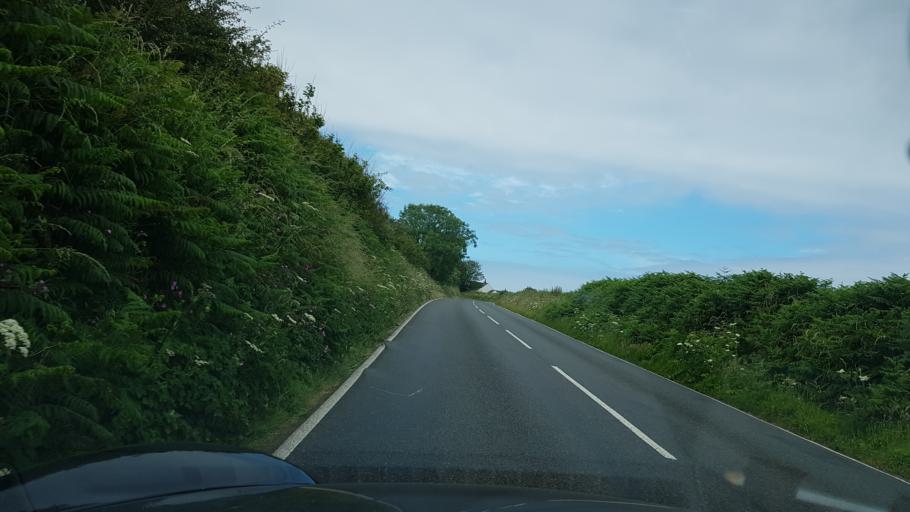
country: GB
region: Wales
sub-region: Pembrokeshire
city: Steynton
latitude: 51.7736
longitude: -5.0480
